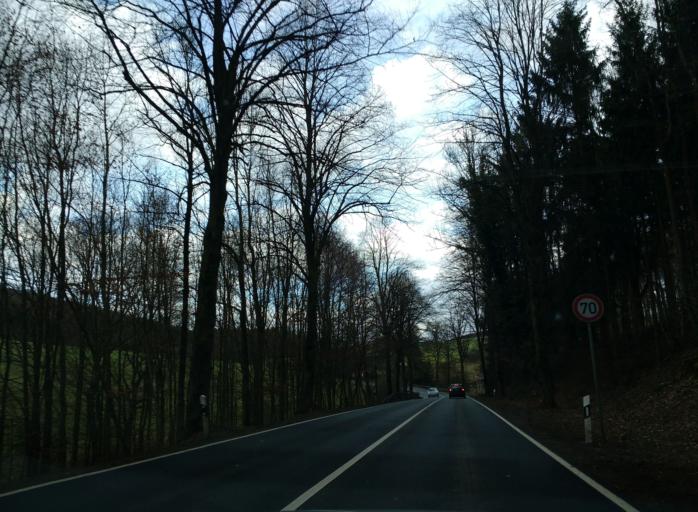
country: DE
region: North Rhine-Westphalia
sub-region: Regierungsbezirk Detmold
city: Lemgo
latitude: 52.0681
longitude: 8.9153
